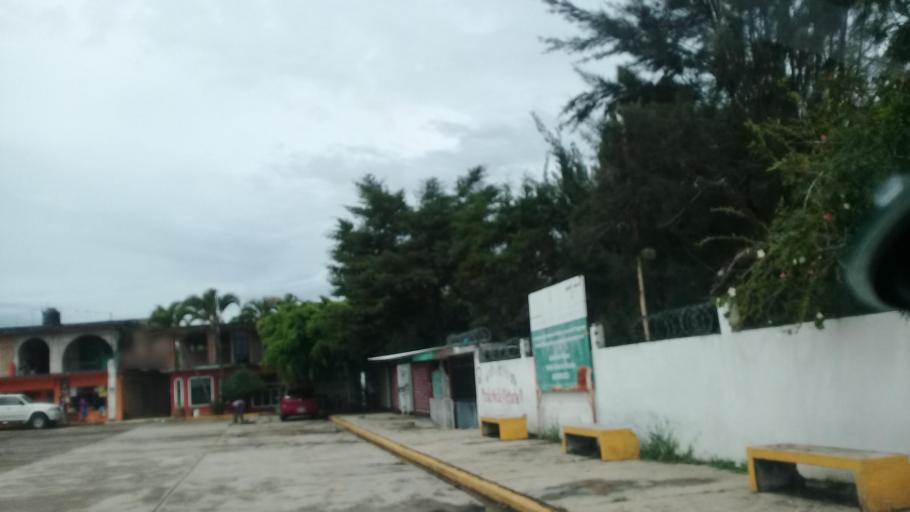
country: MX
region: Veracruz
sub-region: Emiliano Zapata
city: Dos Rios
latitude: 19.4805
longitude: -96.7980
